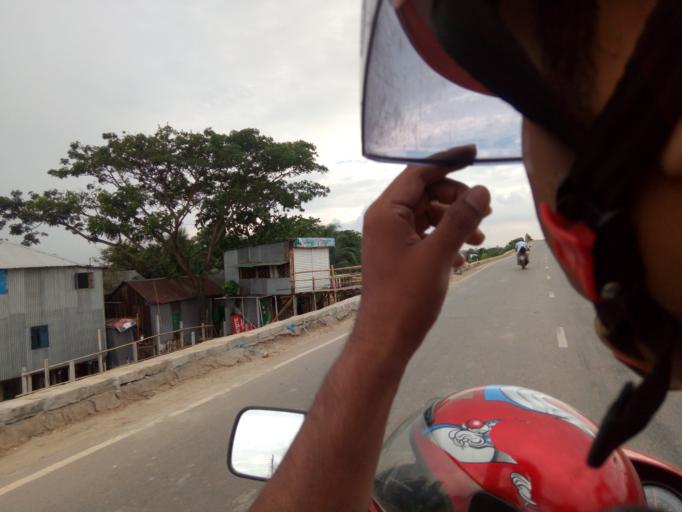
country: BD
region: Dhaka
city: Paltan
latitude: 23.7495
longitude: 90.4611
